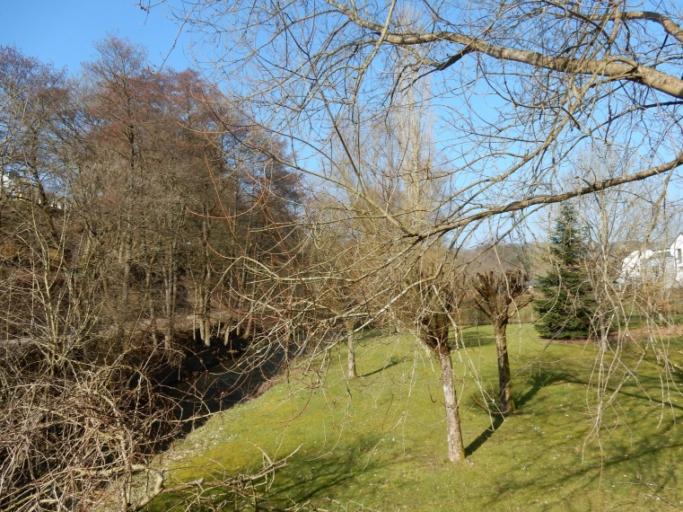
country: LU
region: Diekirch
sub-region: Canton de Wiltz
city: Winseler
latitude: 49.9677
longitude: 5.8903
